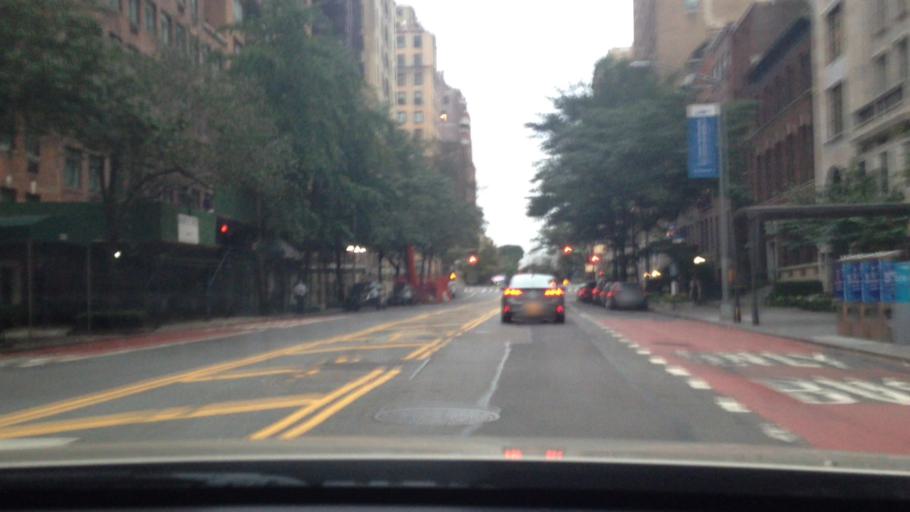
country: US
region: New York
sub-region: New York County
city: Manhattan
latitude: 40.7750
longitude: -73.9591
